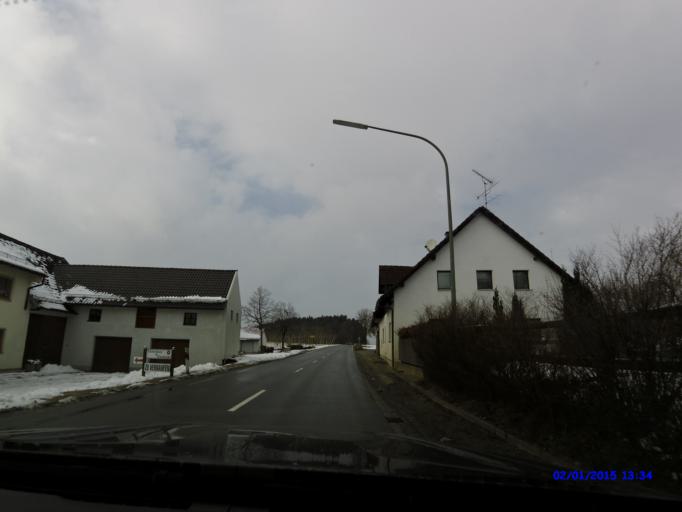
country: DE
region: Bavaria
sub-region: Lower Bavaria
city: Volkenschwand
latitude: 48.5916
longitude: 11.8857
